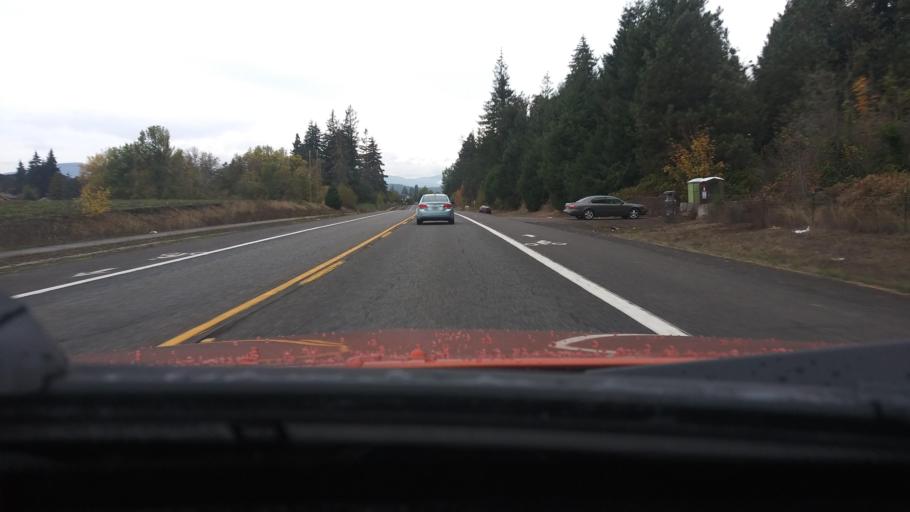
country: US
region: Oregon
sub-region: Washington County
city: Forest Grove
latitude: 45.5294
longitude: -123.0908
